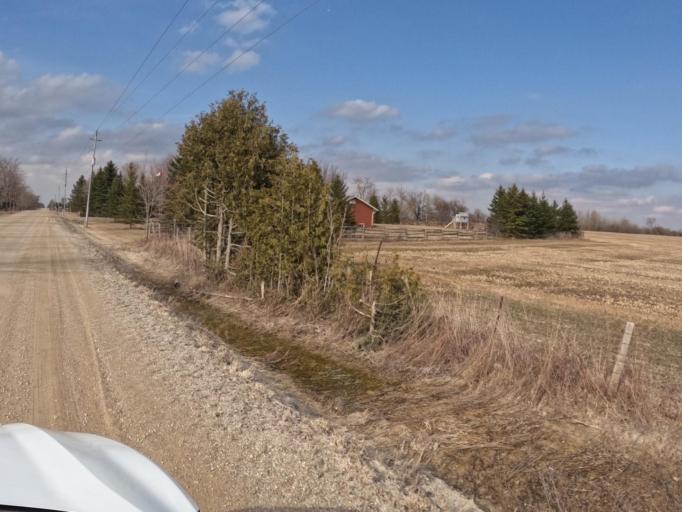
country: CA
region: Ontario
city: Shelburne
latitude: 43.9095
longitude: -80.3034
